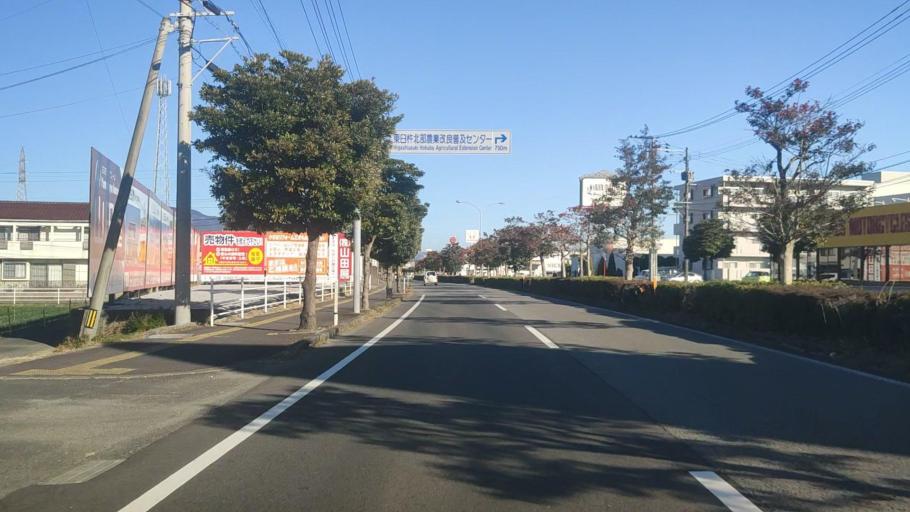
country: JP
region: Miyazaki
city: Nobeoka
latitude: 32.5690
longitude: 131.6835
